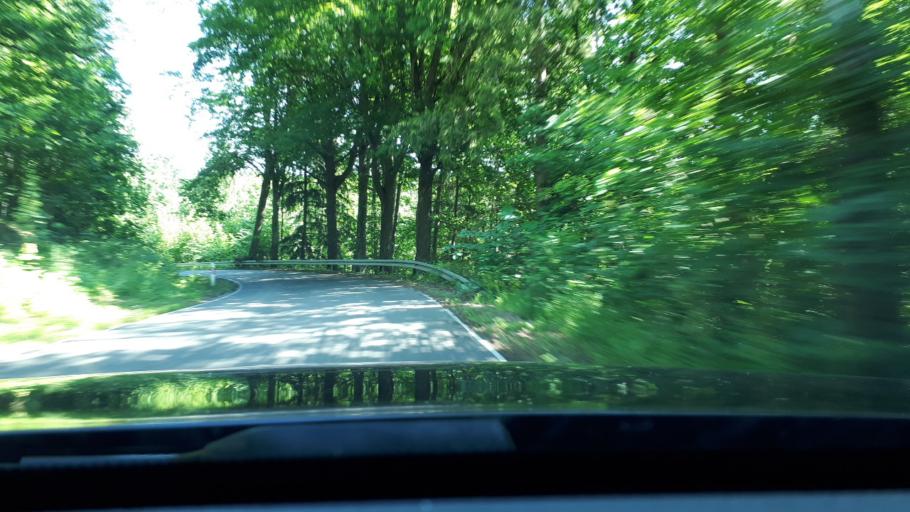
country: PL
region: Warmian-Masurian Voivodeship
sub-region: Powiat ostrodzki
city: Ostroda
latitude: 53.6873
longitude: 20.0767
